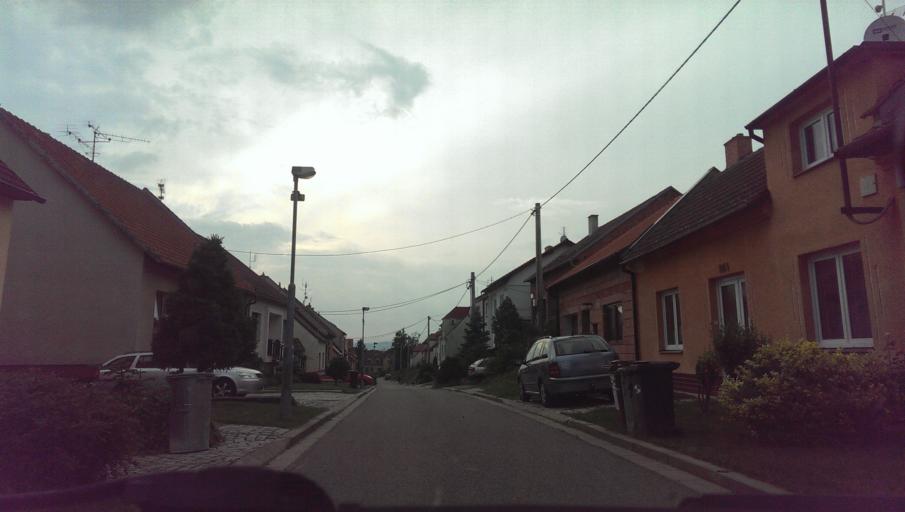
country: CZ
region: Zlin
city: Popovice
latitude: 49.0334
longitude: 17.5106
